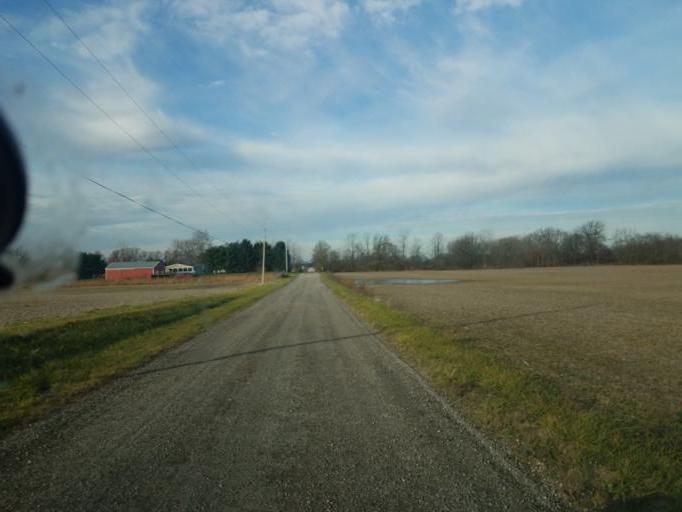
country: US
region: Ohio
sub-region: Morrow County
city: Mount Gilead
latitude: 40.5791
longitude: -82.8785
